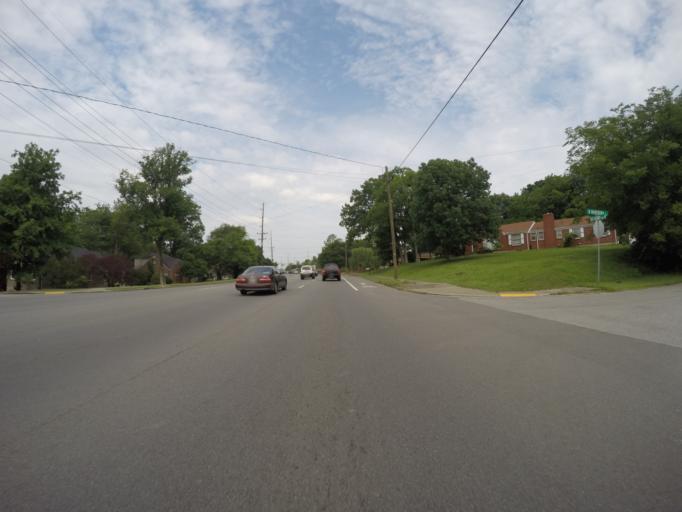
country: US
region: Tennessee
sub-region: Davidson County
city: Goodlettsville
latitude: 36.2645
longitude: -86.7299
